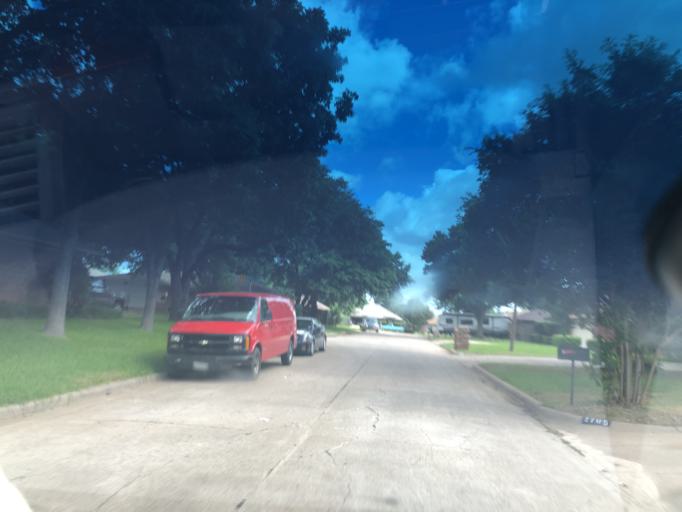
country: US
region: Texas
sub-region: Dallas County
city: Grand Prairie
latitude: 32.7067
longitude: -97.0333
